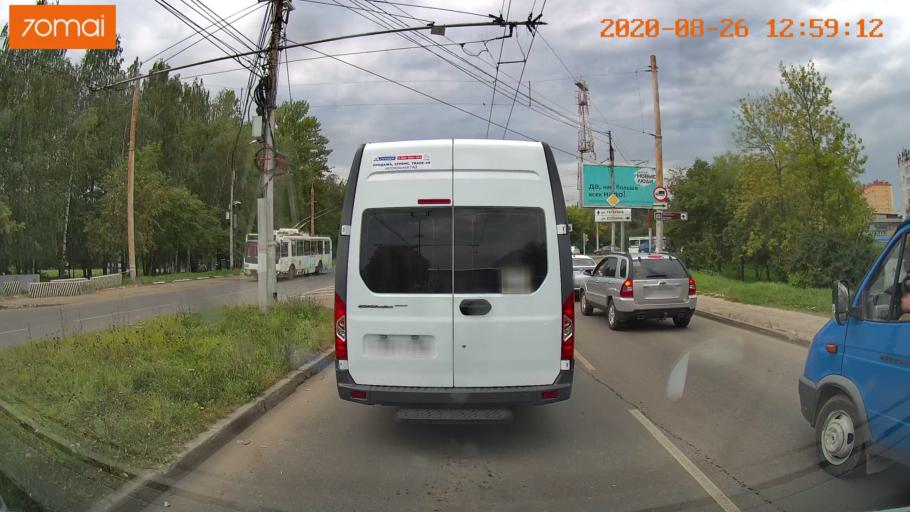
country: RU
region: Rjazan
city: Ryazan'
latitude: 54.6145
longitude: 39.7442
